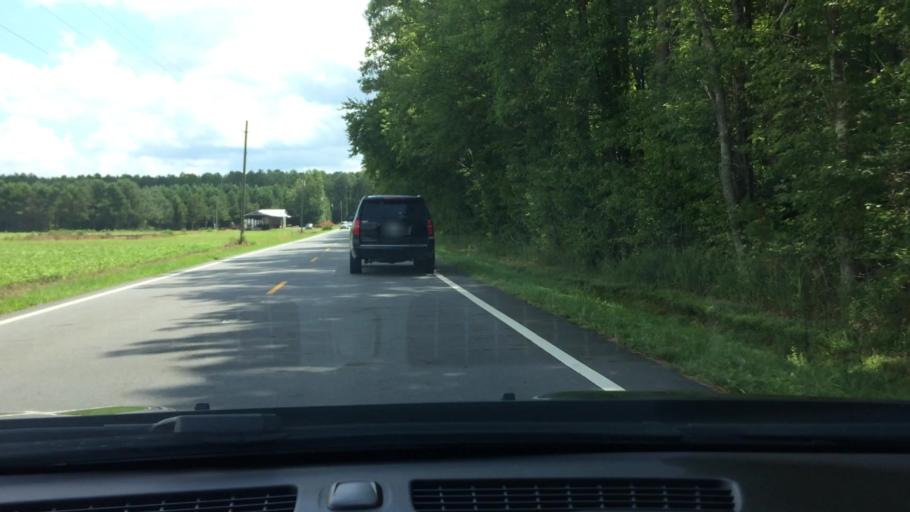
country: US
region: North Carolina
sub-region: Craven County
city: Vanceboro
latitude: 35.4225
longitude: -77.2261
